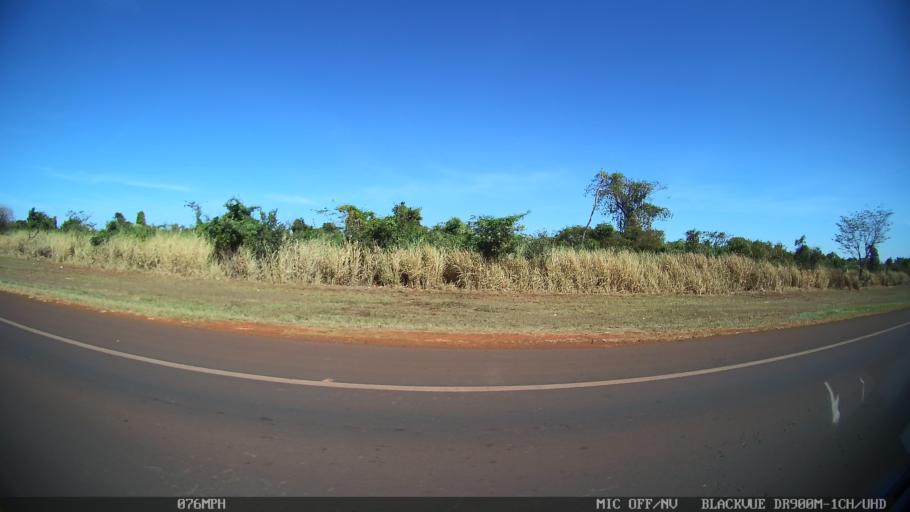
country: BR
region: Sao Paulo
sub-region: Ipua
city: Ipua
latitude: -20.4635
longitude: -48.1343
